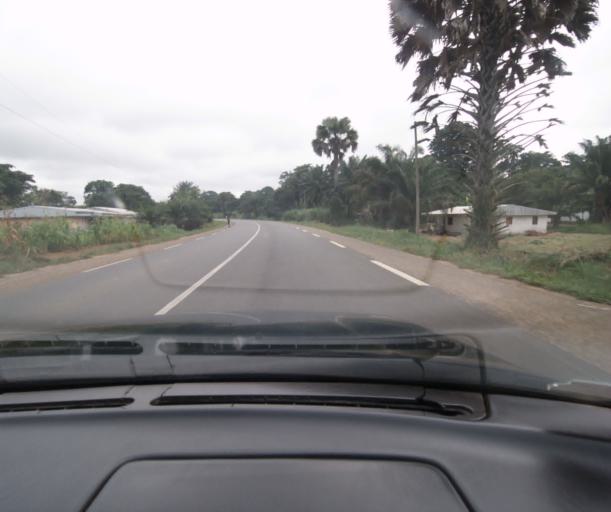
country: CM
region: Centre
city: Saa
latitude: 4.3420
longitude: 11.2839
